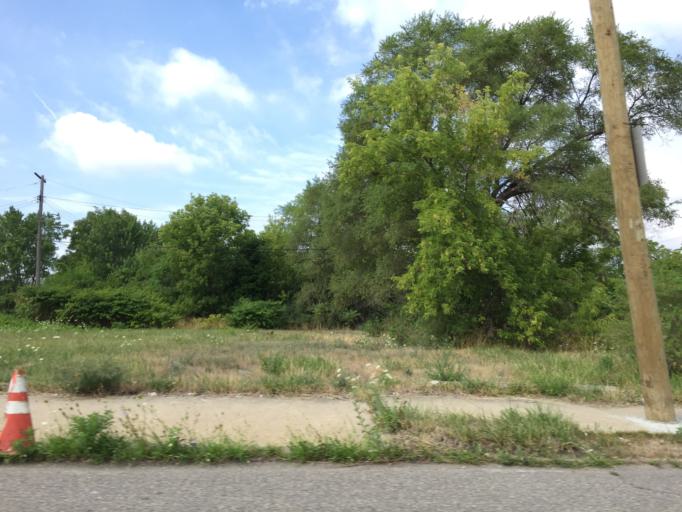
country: US
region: Michigan
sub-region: Wayne County
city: Detroit
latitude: 42.3612
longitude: -83.0379
